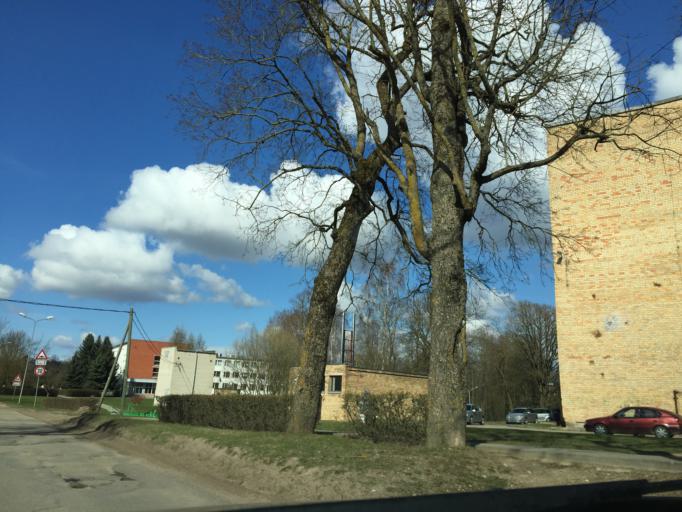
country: LV
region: Kekava
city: Kekava
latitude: 56.8250
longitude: 24.2294
